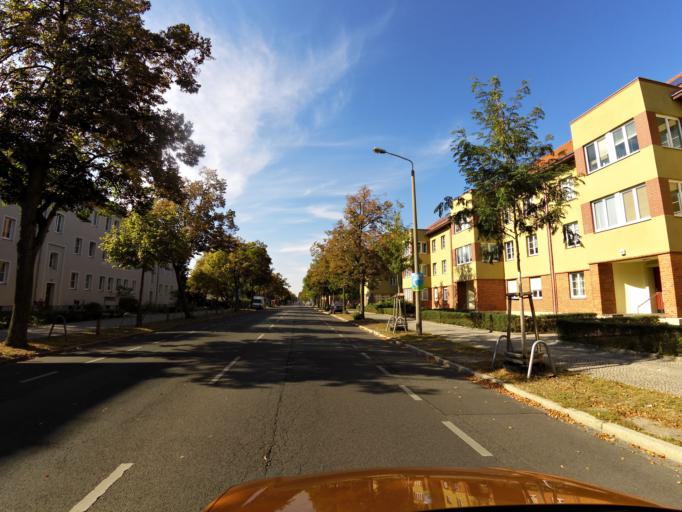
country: DE
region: Brandenburg
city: Potsdam
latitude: 52.3852
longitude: 13.1122
